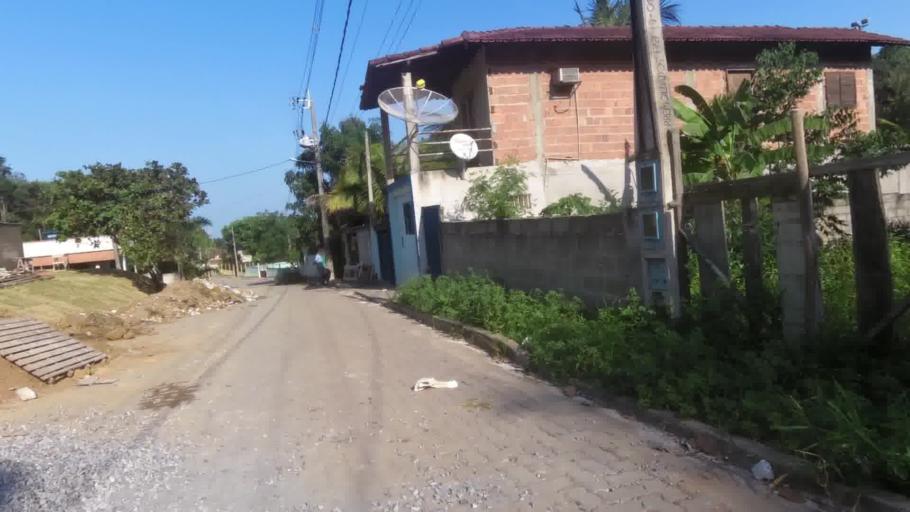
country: BR
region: Espirito Santo
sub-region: Piuma
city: Piuma
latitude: -20.8602
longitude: -40.7603
